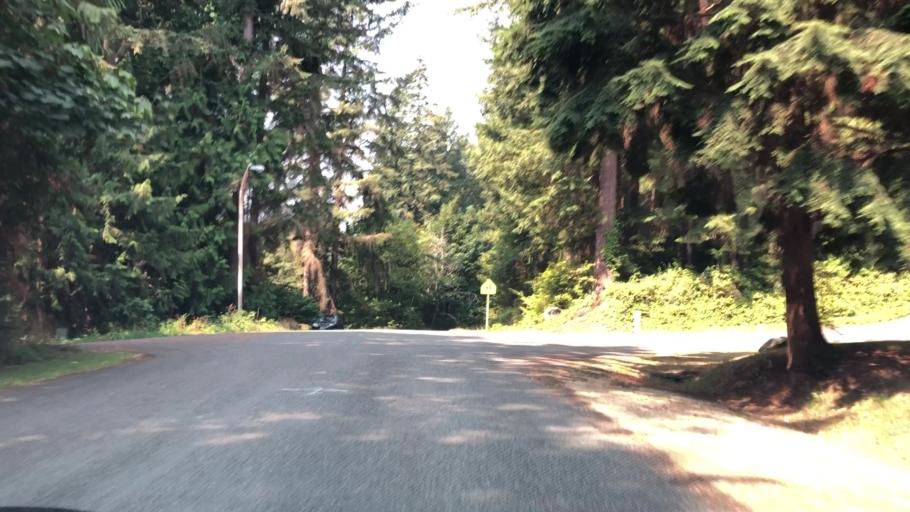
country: US
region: Washington
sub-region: King County
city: Cottage Lake
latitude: 47.7455
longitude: -122.0763
